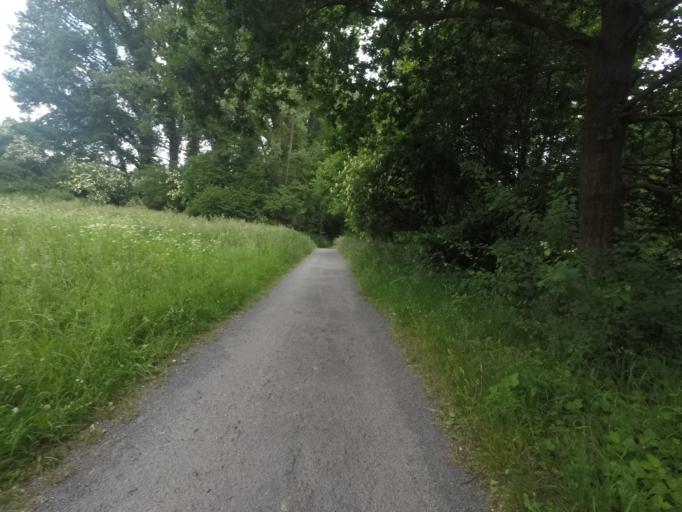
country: DE
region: North Rhine-Westphalia
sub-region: Regierungsbezirk Detmold
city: Hiddenhausen
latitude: 52.1583
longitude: 8.5996
